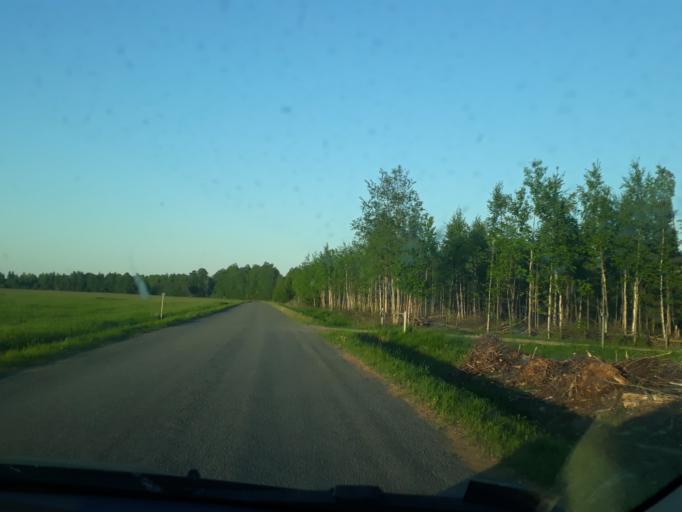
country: EE
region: Paernumaa
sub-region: Vaendra vald (alev)
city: Vandra
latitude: 58.5633
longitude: 24.9614
